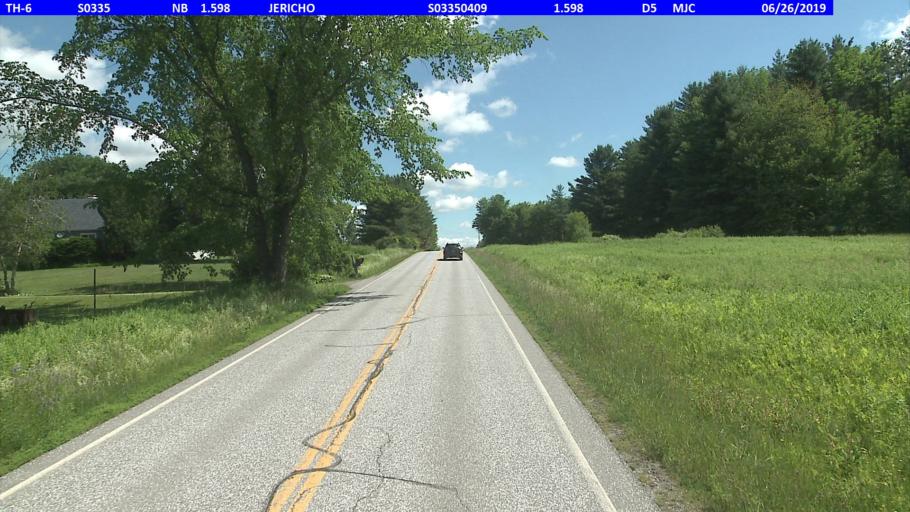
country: US
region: Vermont
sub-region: Chittenden County
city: Jericho
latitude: 44.4865
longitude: -73.0131
